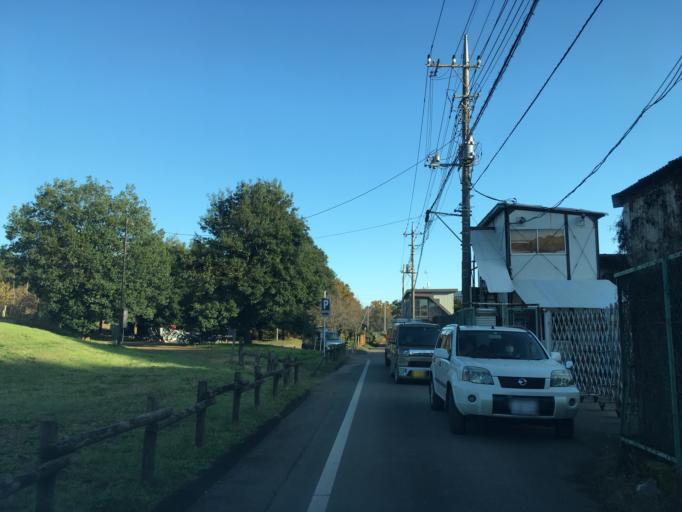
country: JP
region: Saitama
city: Tokorozawa
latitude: 35.8011
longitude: 139.4913
